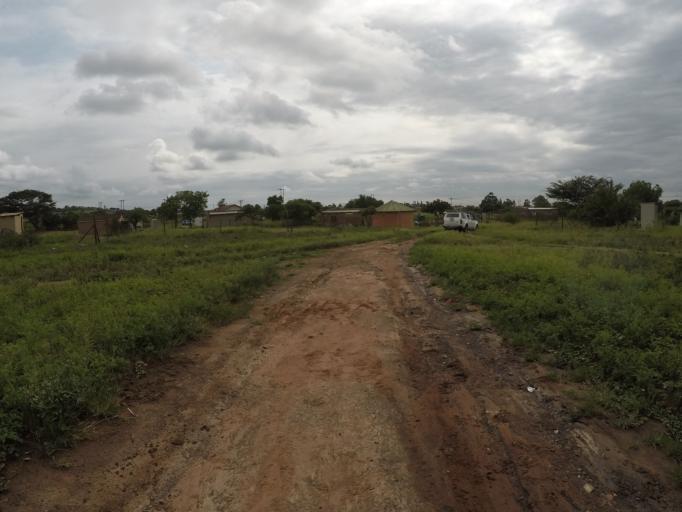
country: ZA
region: KwaZulu-Natal
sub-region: uThungulu District Municipality
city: Empangeni
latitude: -28.7140
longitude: 31.8616
